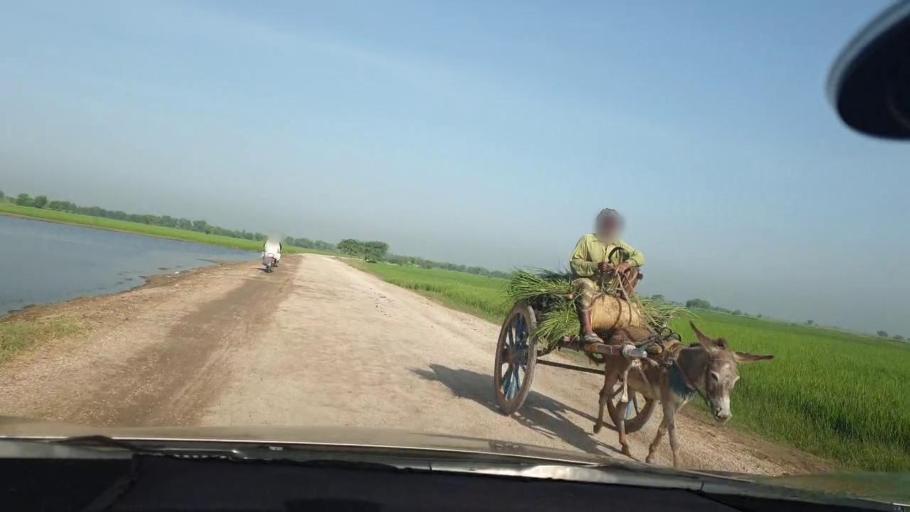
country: PK
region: Sindh
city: Kambar
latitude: 27.6561
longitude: 68.0288
